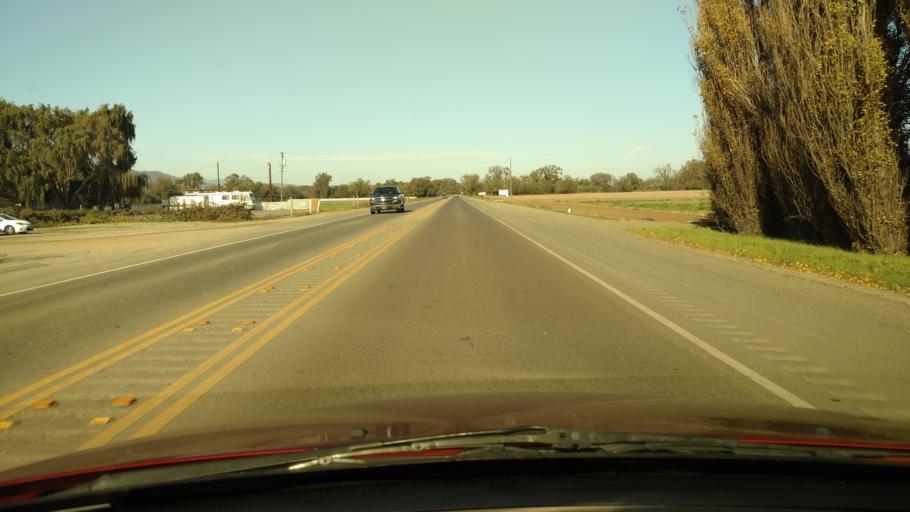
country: US
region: California
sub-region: Santa Clara County
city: Gilroy
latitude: 36.9559
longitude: -121.5305
